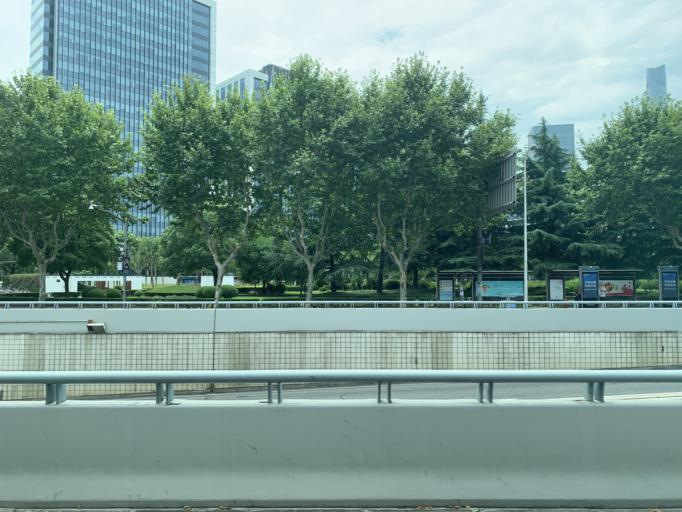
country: CN
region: Shanghai Shi
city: Pudong
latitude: 31.2333
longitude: 121.5201
